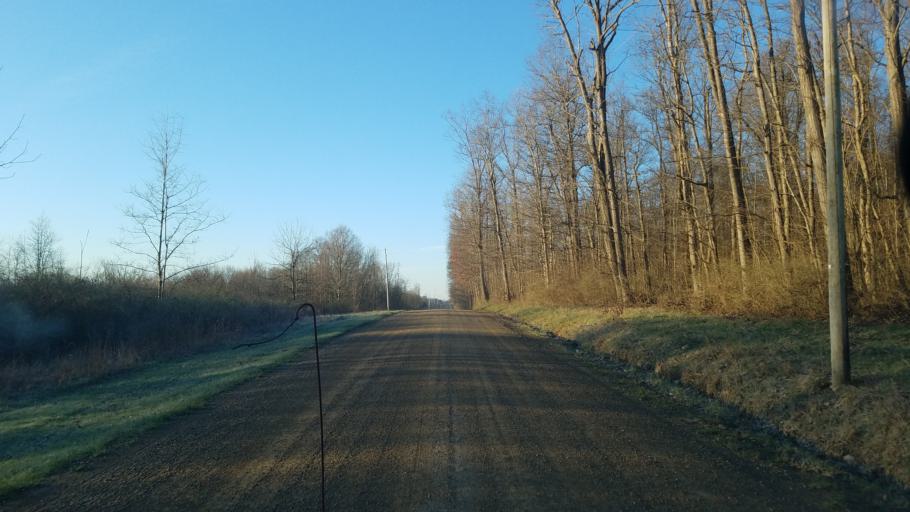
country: US
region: Ohio
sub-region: Knox County
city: Oak Hill
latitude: 40.3285
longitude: -82.2106
